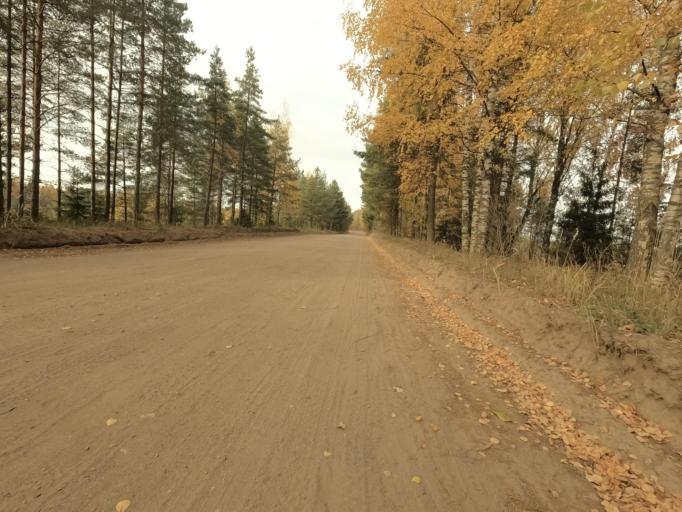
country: RU
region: Leningrad
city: Priladozhskiy
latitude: 59.6750
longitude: 31.3663
